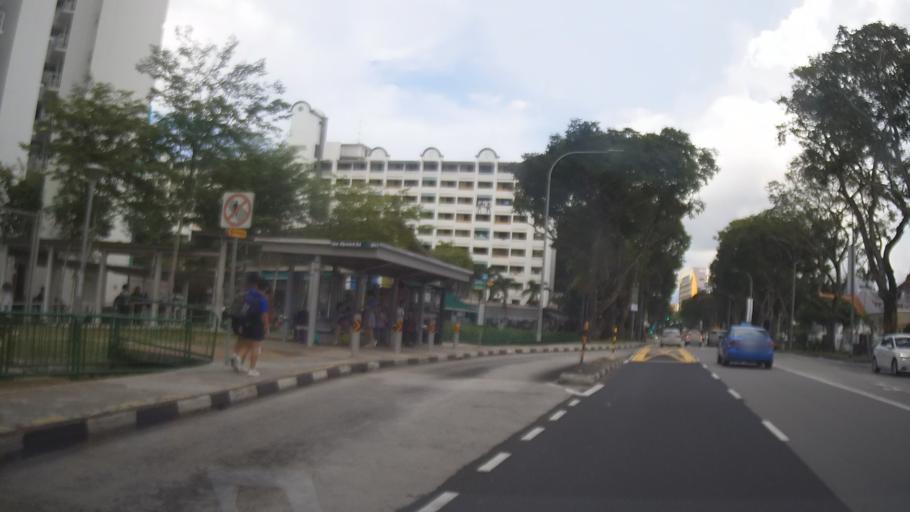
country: SG
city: Singapore
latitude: 1.3350
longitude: 103.8781
